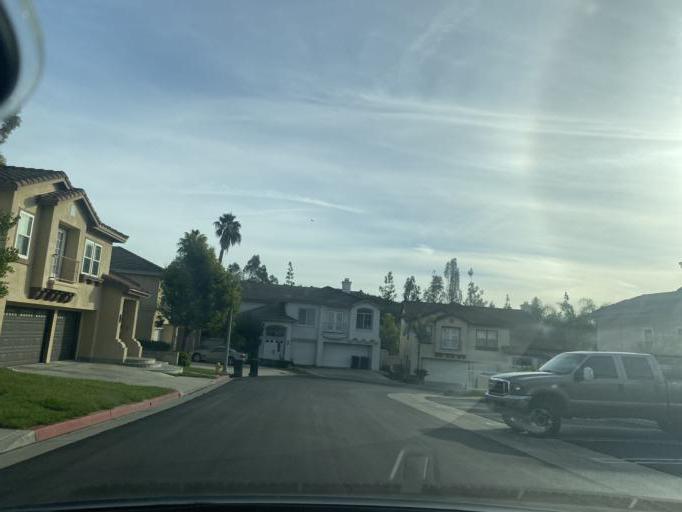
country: US
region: California
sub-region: Orange County
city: Brea
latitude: 33.9005
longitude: -117.9013
